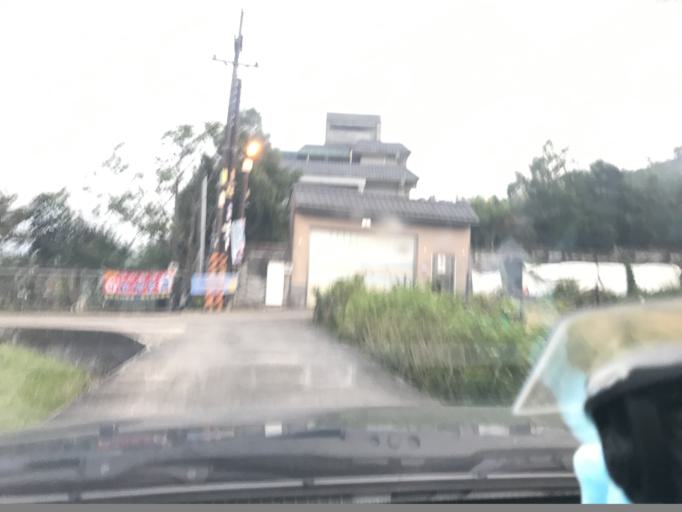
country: TW
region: Taiwan
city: Daxi
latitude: 24.8465
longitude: 121.2117
